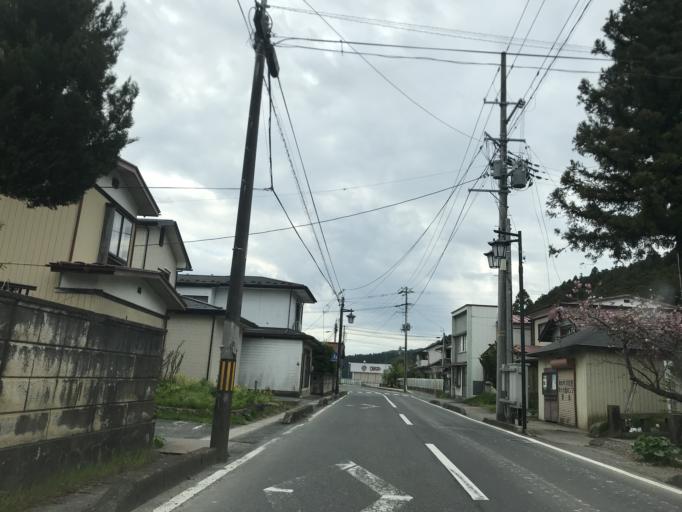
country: JP
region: Iwate
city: Ichinoseki
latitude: 38.7673
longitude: 141.3280
